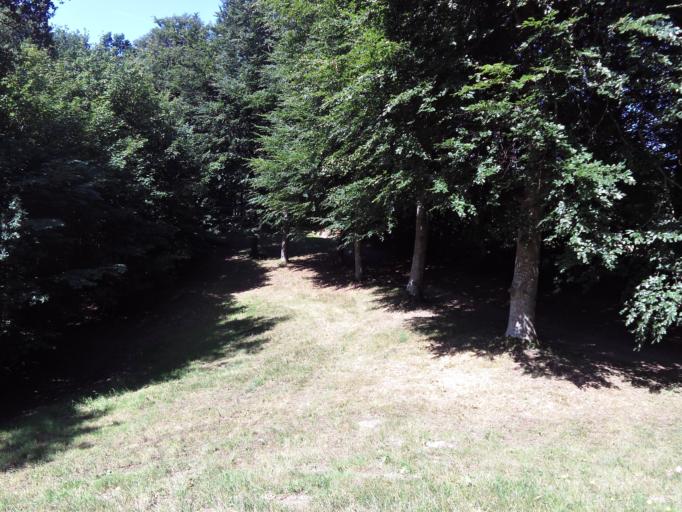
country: DK
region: South Denmark
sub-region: Vejen Kommune
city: Vejen
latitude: 55.4475
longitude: 9.1147
